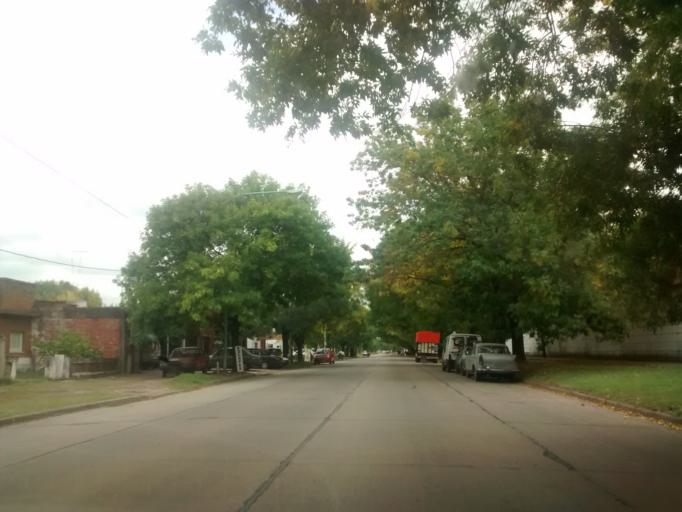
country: AR
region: Buenos Aires
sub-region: Partido de La Plata
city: La Plata
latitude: -34.9570
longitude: -57.9494
